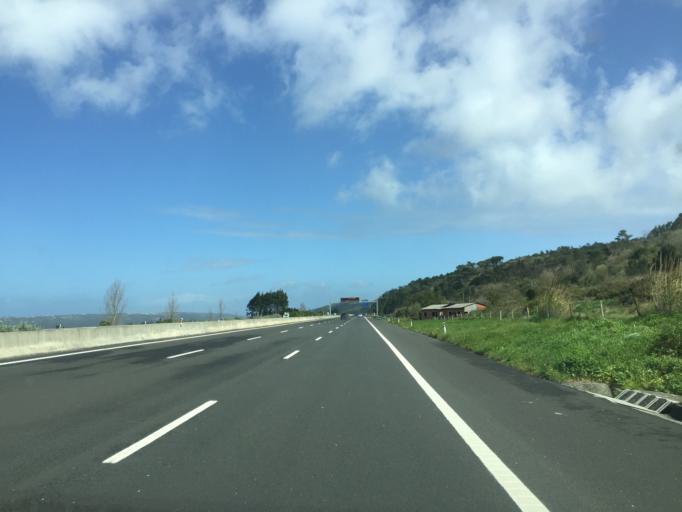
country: PT
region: Leiria
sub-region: Caldas da Rainha
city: Caldas da Rainha
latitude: 39.4798
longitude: -9.1009
